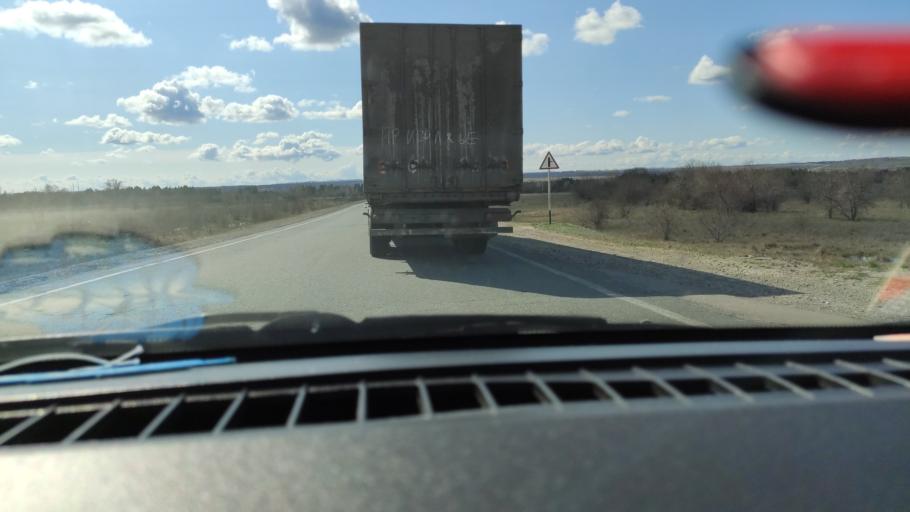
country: RU
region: Samara
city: Varlamovo
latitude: 53.1577
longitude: 48.2843
